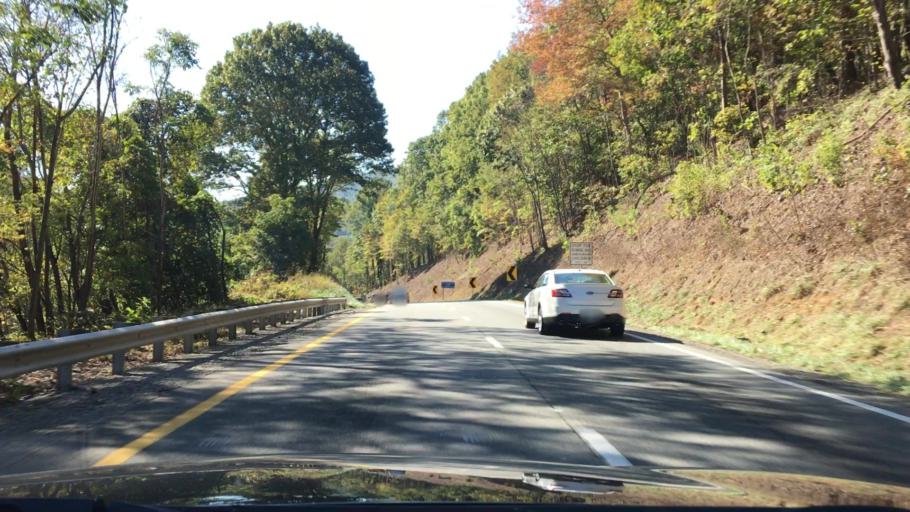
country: US
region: Virginia
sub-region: Roanoke County
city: Narrows
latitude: 37.1396
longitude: -79.9727
